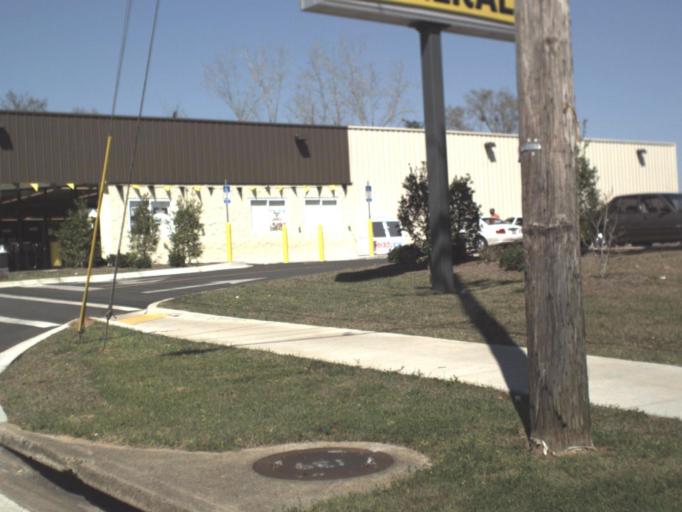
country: US
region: Florida
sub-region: Leon County
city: Tallahassee
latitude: 30.4209
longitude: -84.3023
